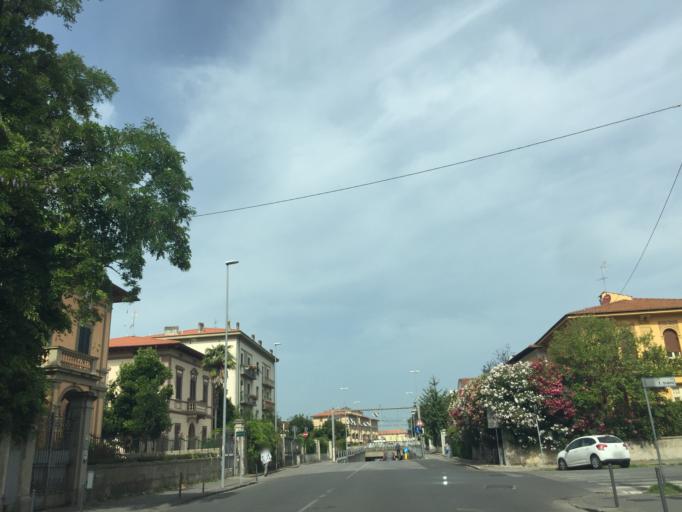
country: IT
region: Tuscany
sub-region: Province of Pisa
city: Pisa
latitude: 43.7192
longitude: 10.3891
